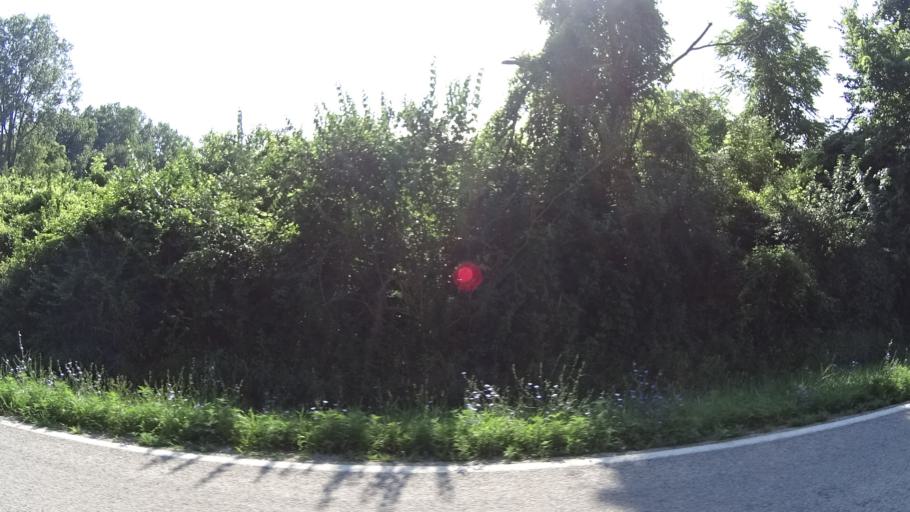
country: US
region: Ohio
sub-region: Huron County
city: Bellevue
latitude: 41.4063
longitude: -82.8466
